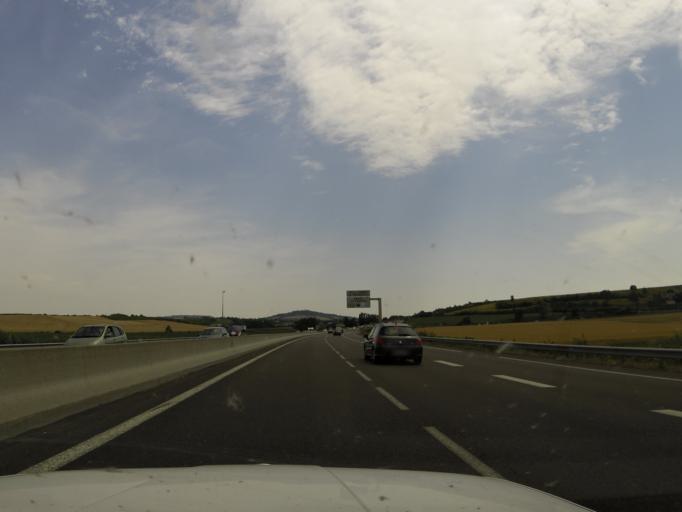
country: FR
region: Auvergne
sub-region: Departement du Puy-de-Dome
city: Perignat-les-Sarlieve
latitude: 45.7277
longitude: 3.1554
